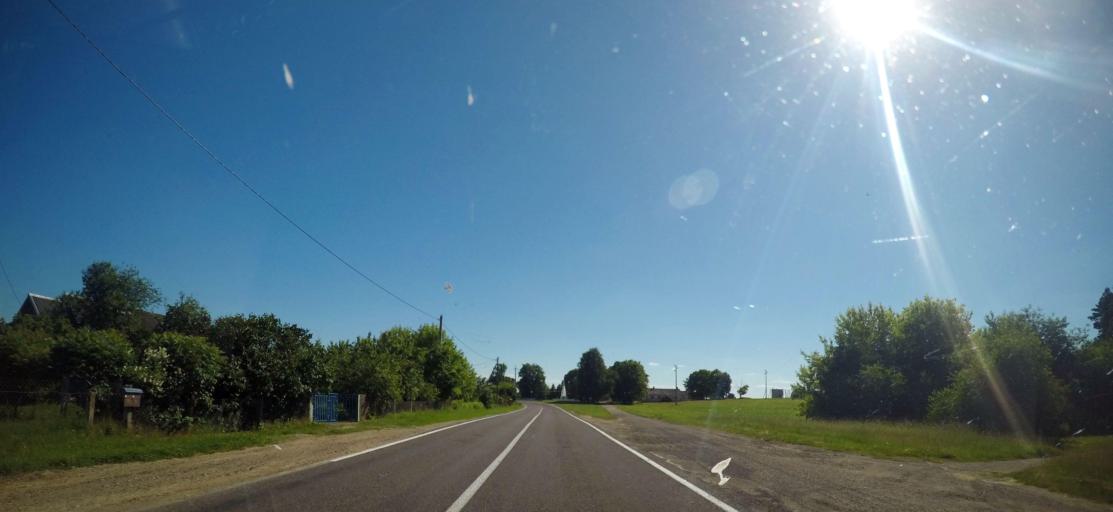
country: BY
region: Grodnenskaya
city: Vyalikaya Byerastavitsa
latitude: 53.1622
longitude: 23.9870
